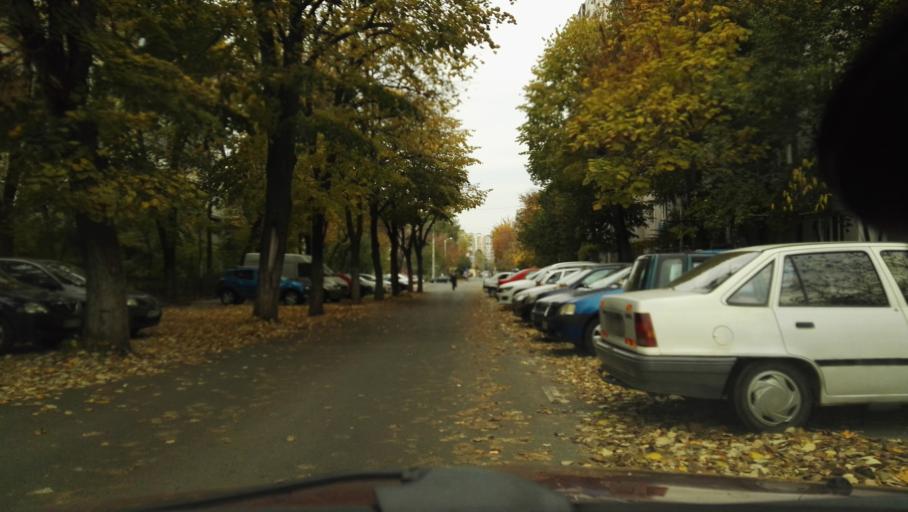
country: RO
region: Bucuresti
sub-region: Municipiul Bucuresti
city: Bucuresti
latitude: 44.3909
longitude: 26.1128
